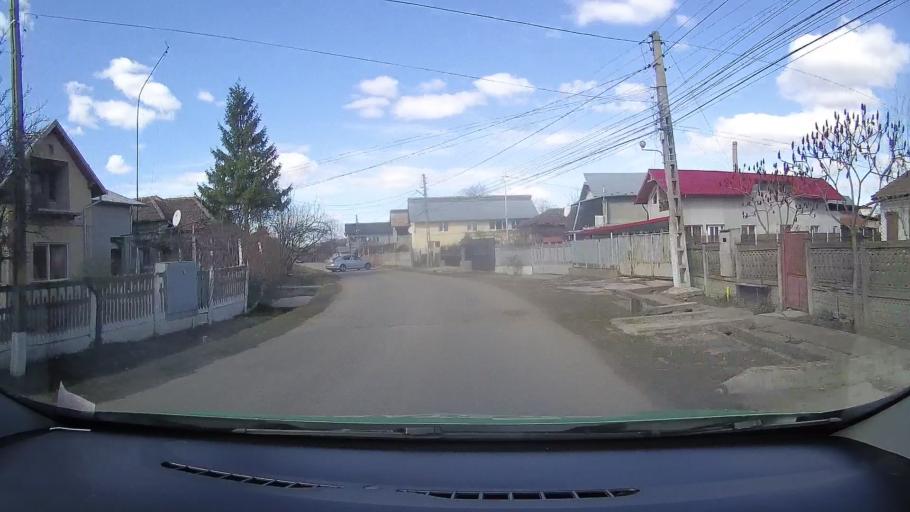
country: RO
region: Dambovita
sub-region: Comuna Doicesti
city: Doicesti
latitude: 44.9916
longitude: 25.3988
